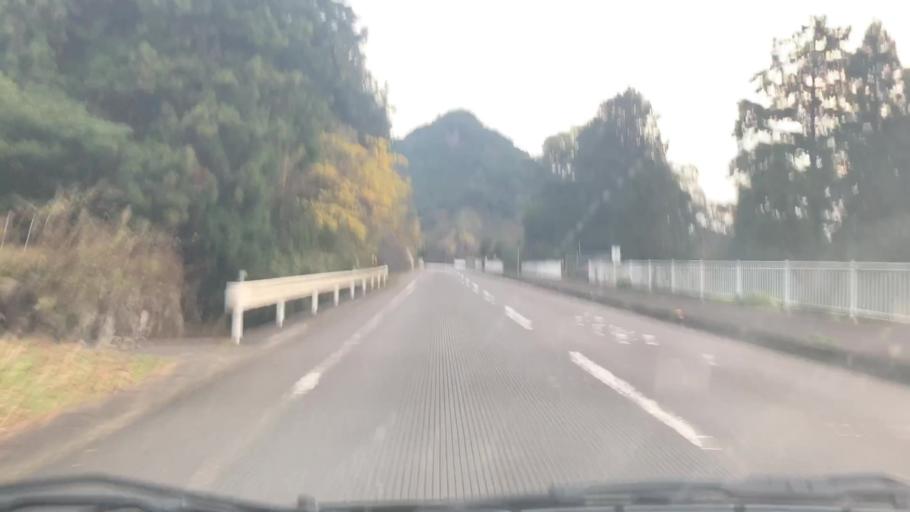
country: JP
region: Saga Prefecture
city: Kashima
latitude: 33.0536
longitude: 130.0722
